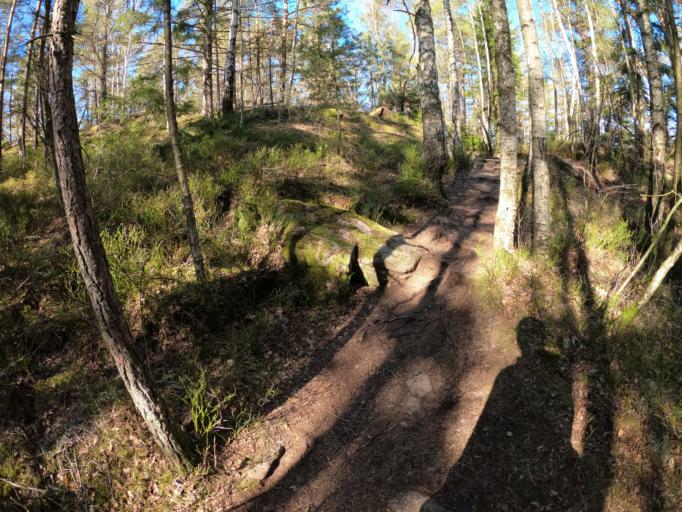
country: SE
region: Vaestra Goetaland
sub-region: Harryda Kommun
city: Molnlycke
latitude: 57.6393
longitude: 12.1140
